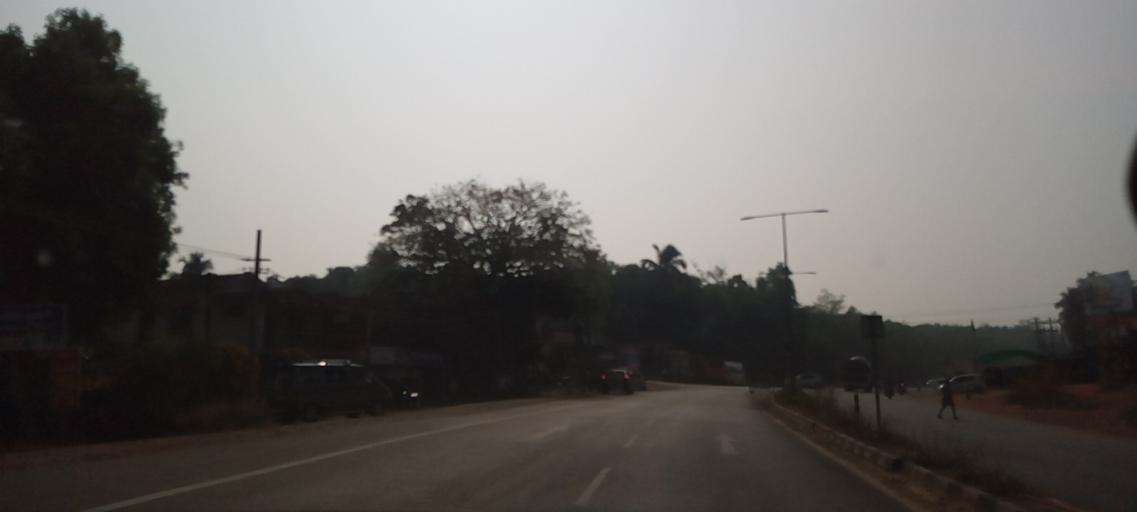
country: IN
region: Karnataka
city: Gangolli
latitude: 13.6778
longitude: 74.6984
